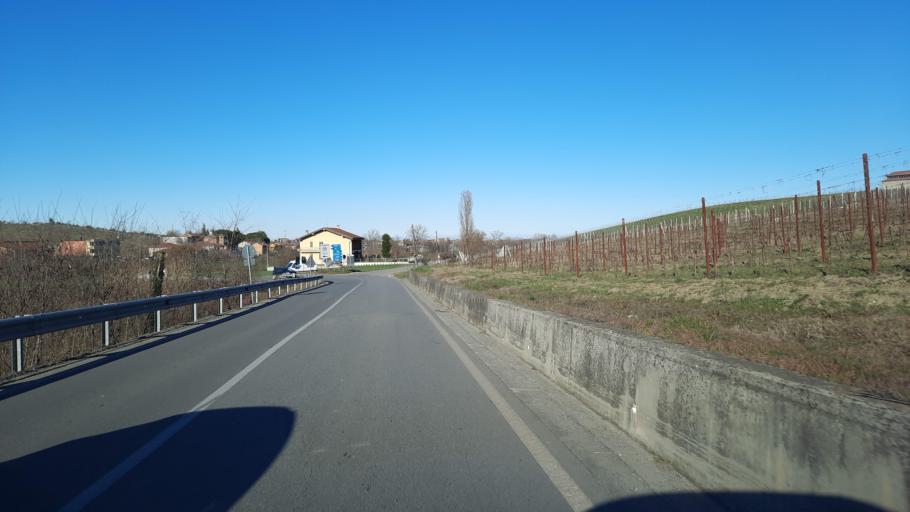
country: IT
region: Piedmont
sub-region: Provincia di Alessandria
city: San Giorgio Monferrato
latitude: 45.1018
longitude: 8.4341
